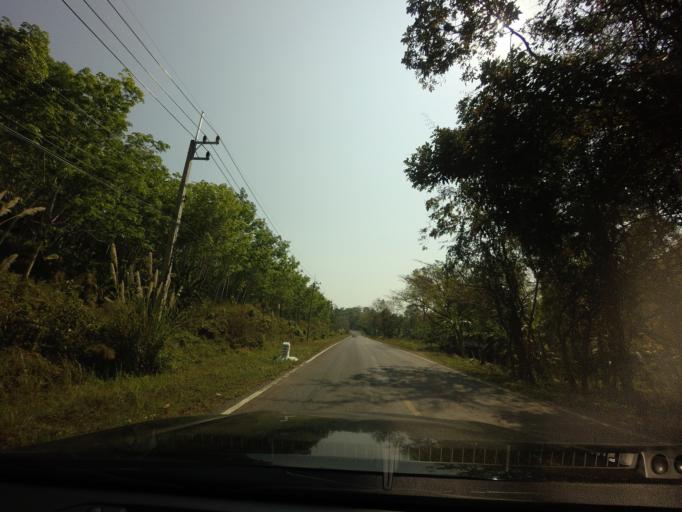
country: TH
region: Kanchanaburi
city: Thong Pha Phum
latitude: 14.6535
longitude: 98.5504
